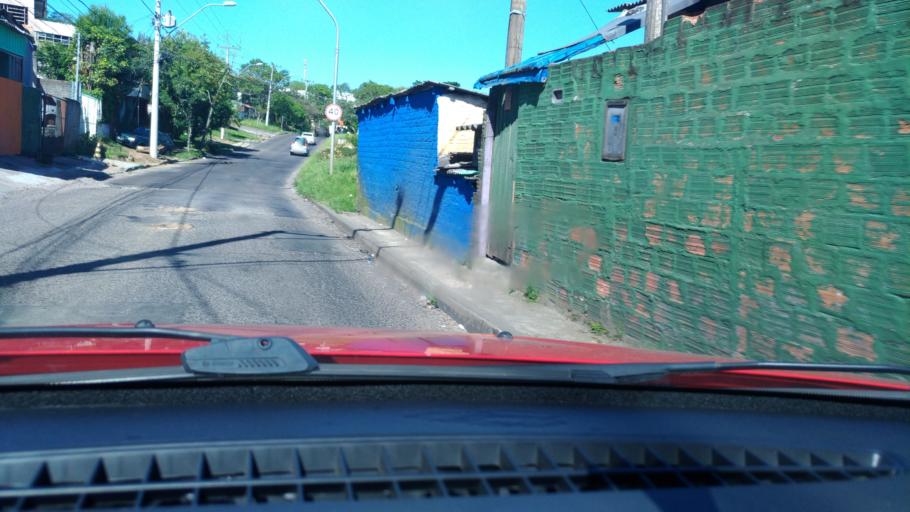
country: BR
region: Rio Grande do Sul
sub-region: Porto Alegre
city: Porto Alegre
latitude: -30.0329
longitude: -51.1481
